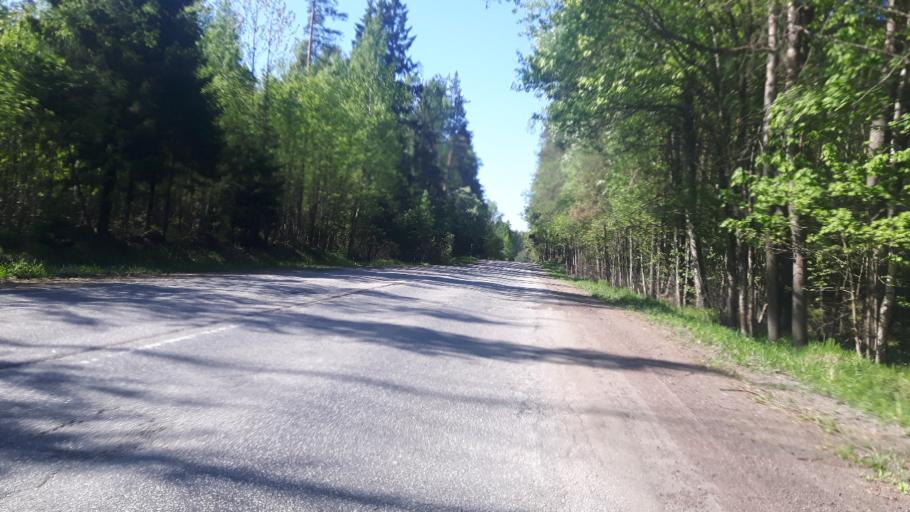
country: RU
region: Leningrad
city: Vyborg
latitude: 60.6422
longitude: 28.7418
